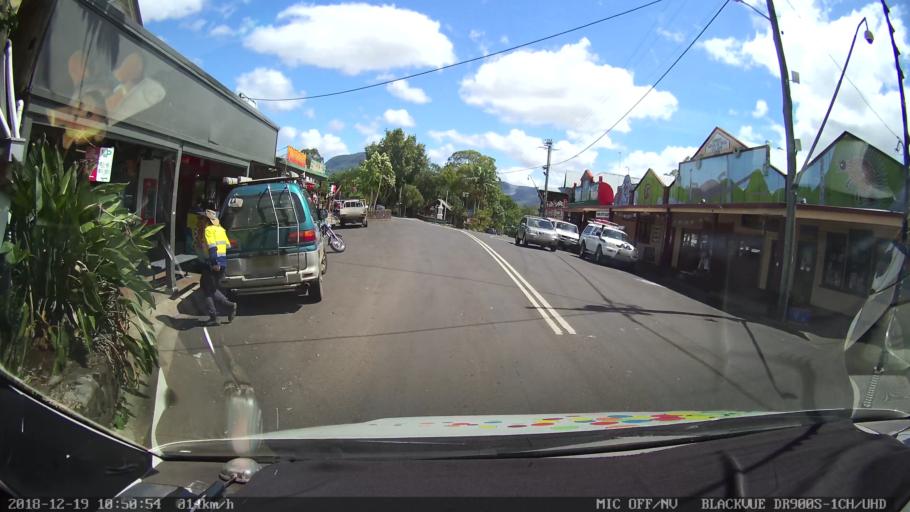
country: AU
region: New South Wales
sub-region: Lismore Municipality
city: Nimbin
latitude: -28.5963
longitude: 153.2230
